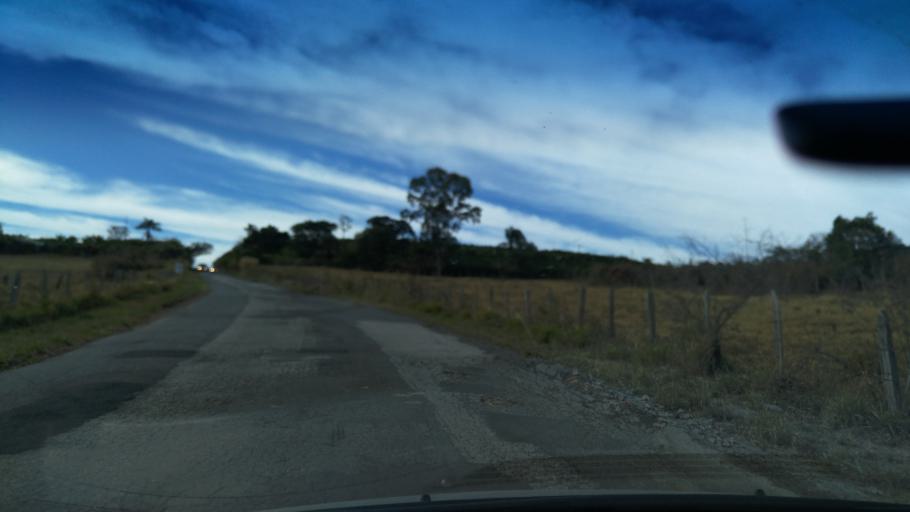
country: BR
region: Minas Gerais
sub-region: Andradas
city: Andradas
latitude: -22.0613
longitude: -46.3913
